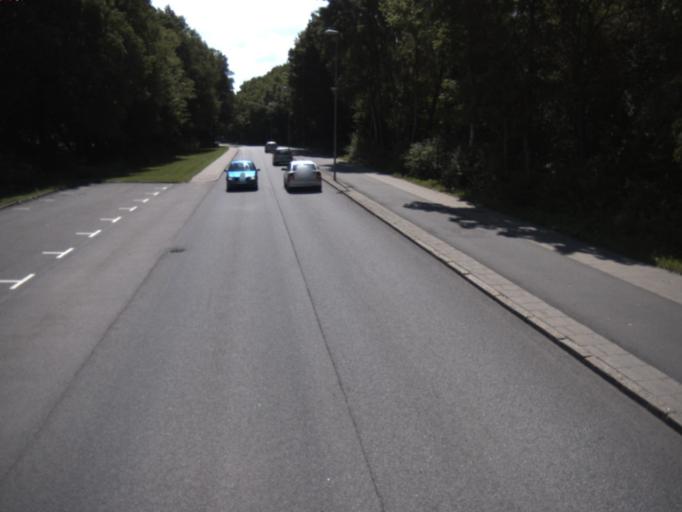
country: SE
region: Skane
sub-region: Helsingborg
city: Helsingborg
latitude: 56.0690
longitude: 12.6929
